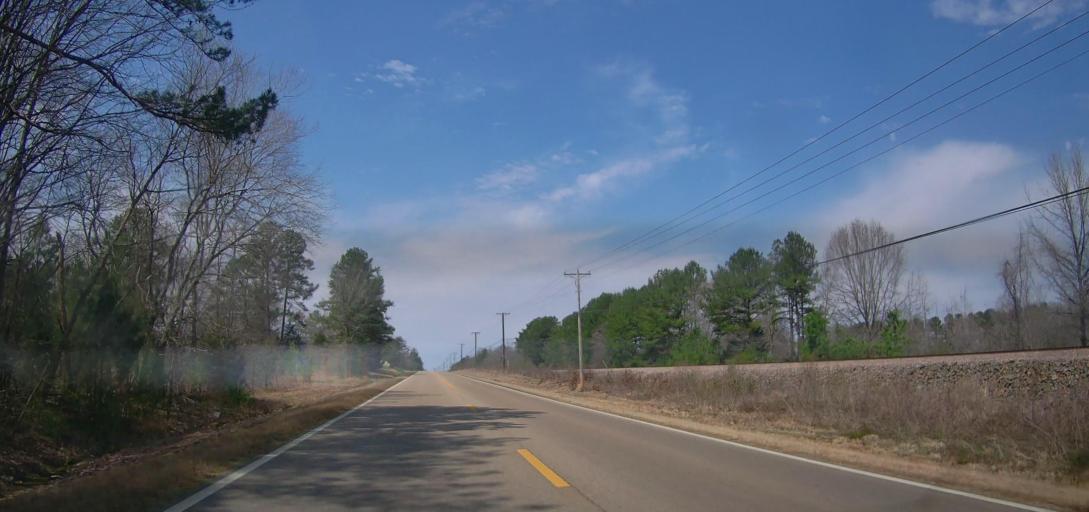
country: US
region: Mississippi
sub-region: Union County
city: New Albany
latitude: 34.5268
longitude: -89.0680
